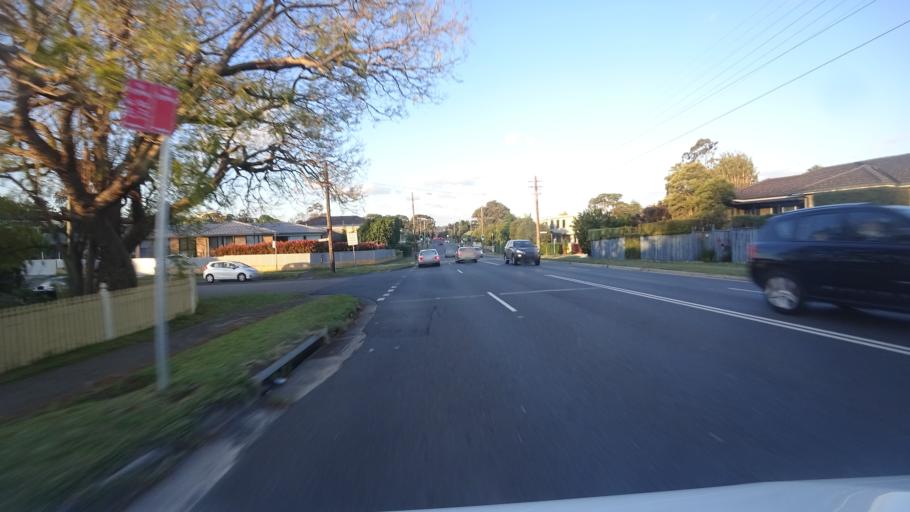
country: AU
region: New South Wales
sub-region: Ryde
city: North Ryde
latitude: -33.7939
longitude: 151.1274
